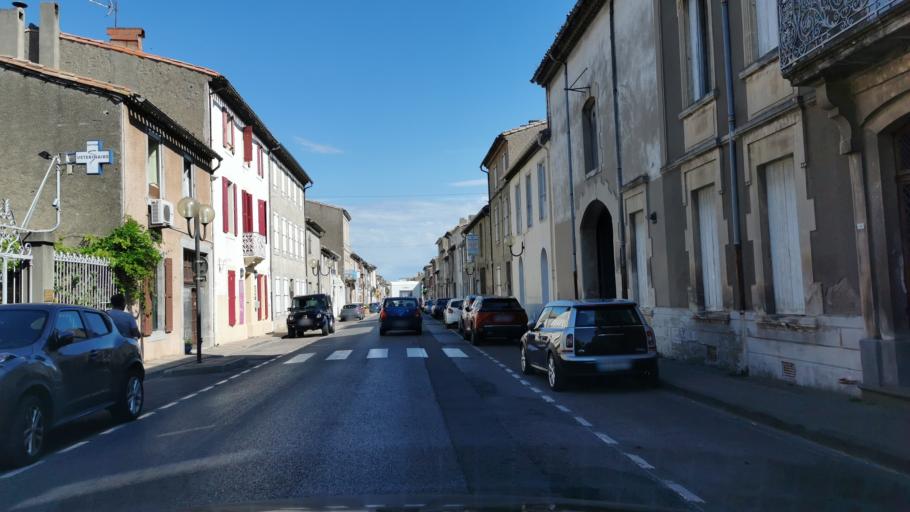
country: FR
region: Languedoc-Roussillon
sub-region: Departement de l'Aude
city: Rieux-Minervois
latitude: 43.2828
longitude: 2.5827
